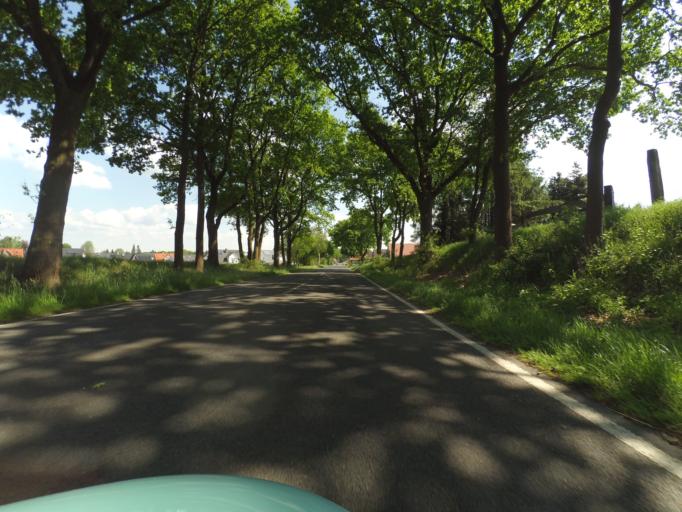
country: DE
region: Lower Saxony
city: Isernhagen Farster Bauerschaft
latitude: 52.5060
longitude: 9.9170
